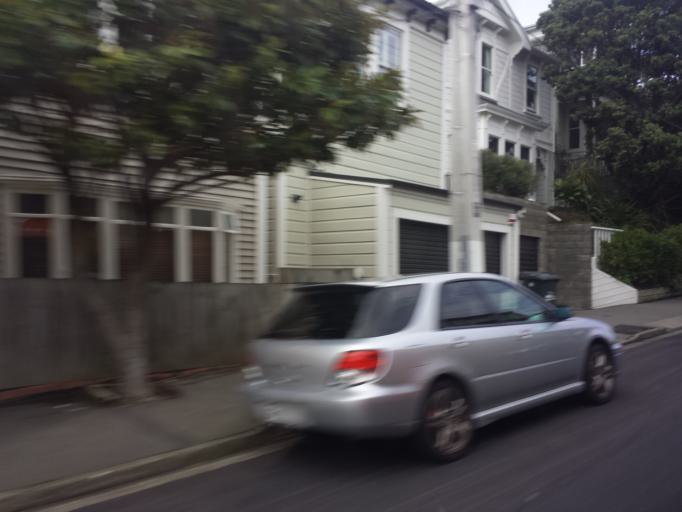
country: NZ
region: Wellington
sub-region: Wellington City
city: Wellington
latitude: -41.2974
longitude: 174.7849
